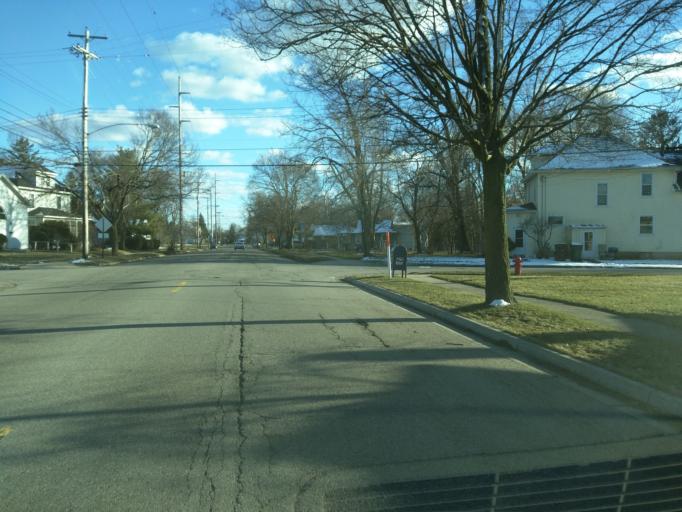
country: US
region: Michigan
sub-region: Ingham County
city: Lansing
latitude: 42.7603
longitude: -84.5545
